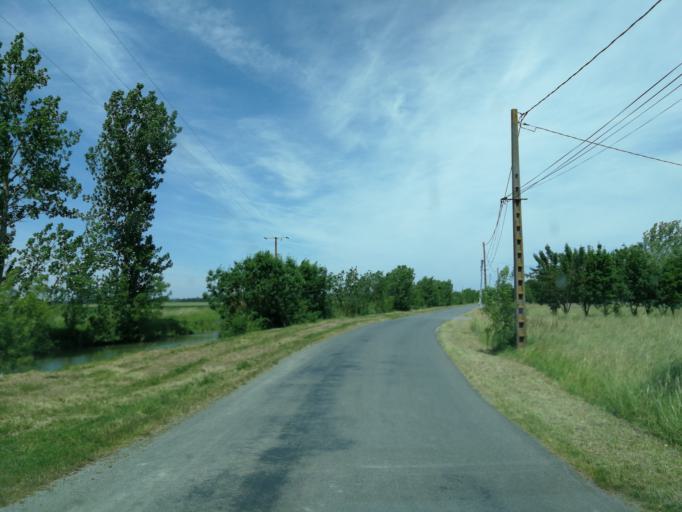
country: FR
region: Pays de la Loire
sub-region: Departement de la Vendee
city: Le Langon
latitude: 46.3890
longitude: -0.9385
